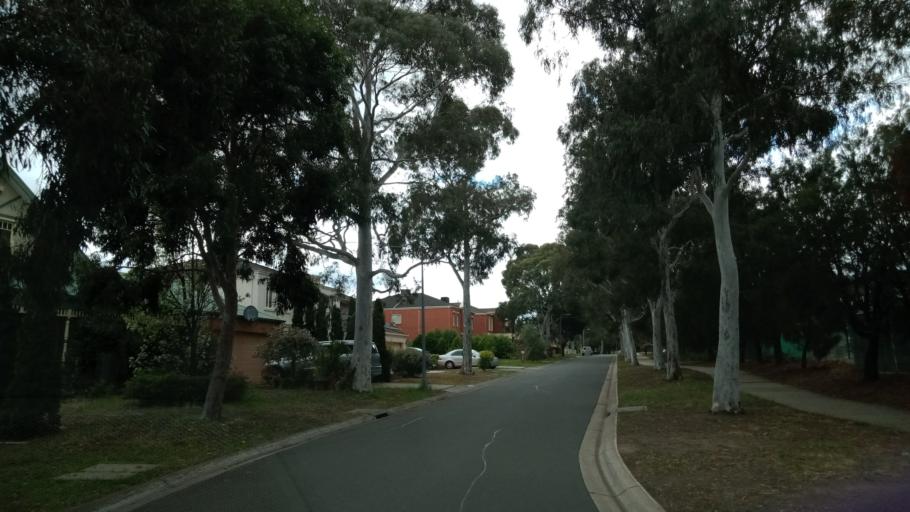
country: AU
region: Victoria
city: Burwood East
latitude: -37.8688
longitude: 145.1598
